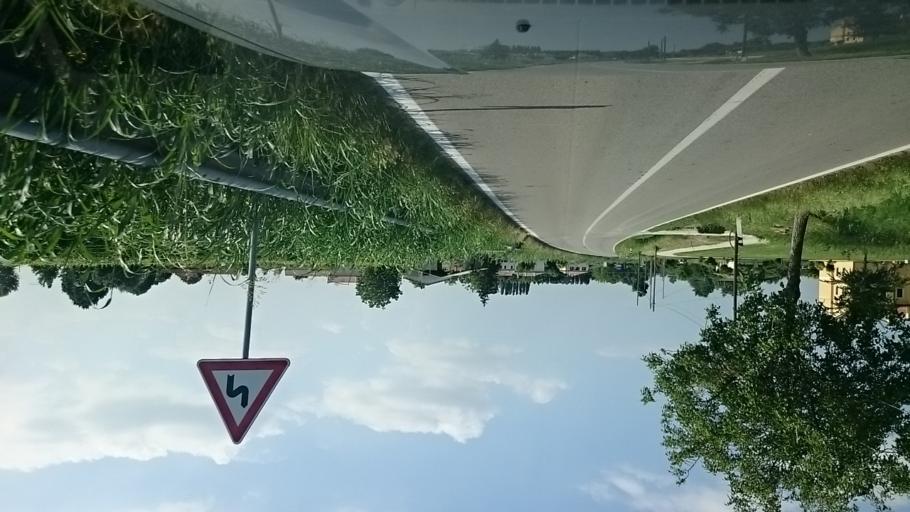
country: IT
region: Veneto
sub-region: Provincia di Padova
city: Villa del Conte
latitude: 45.5667
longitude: 11.8656
